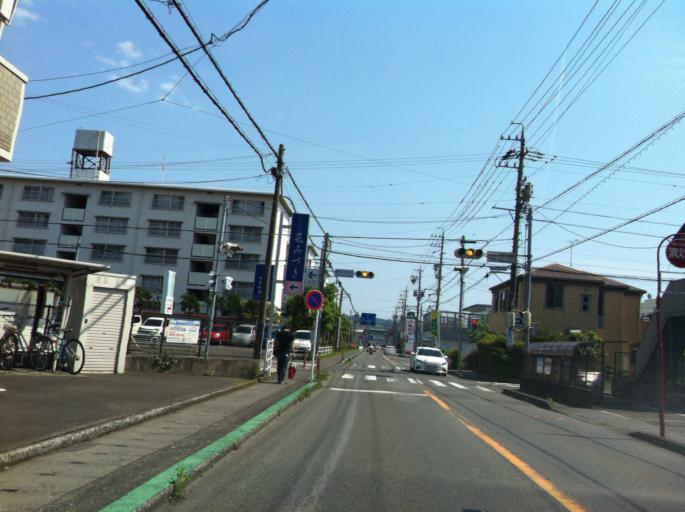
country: JP
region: Shizuoka
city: Shizuoka-shi
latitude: 35.0133
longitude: 138.4239
